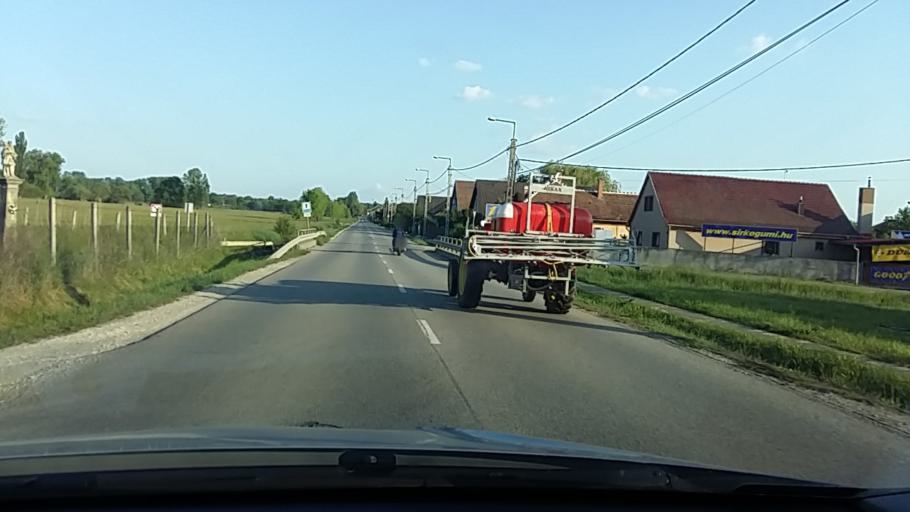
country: HU
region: Pest
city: Szod
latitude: 47.7198
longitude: 19.2305
